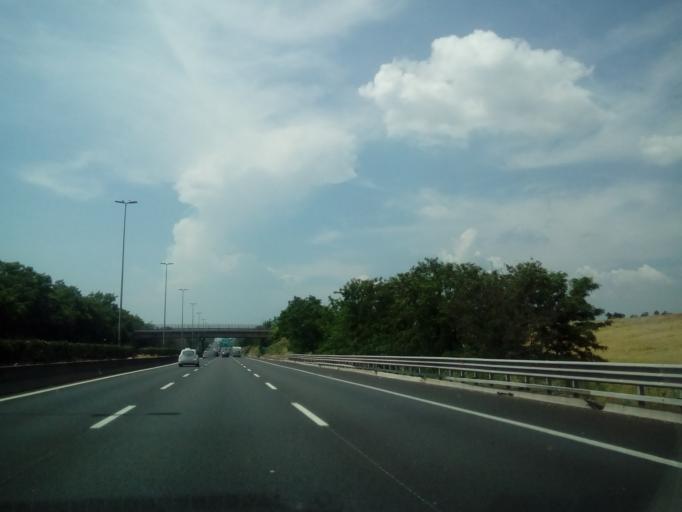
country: IT
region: Latium
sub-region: Citta metropolitana di Roma Capitale
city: Colle Verde
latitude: 41.9652
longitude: 12.5662
